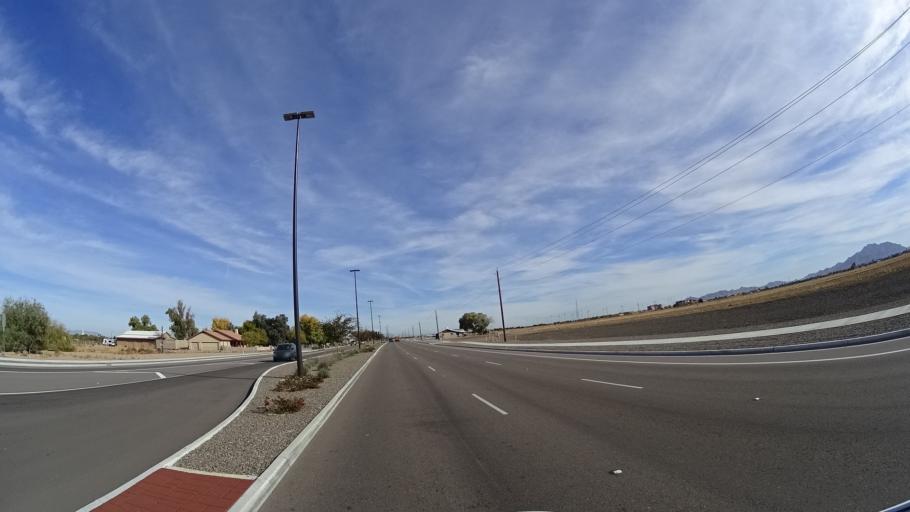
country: US
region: Arizona
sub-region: Maricopa County
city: Gilbert
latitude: 33.2776
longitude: -111.7543
